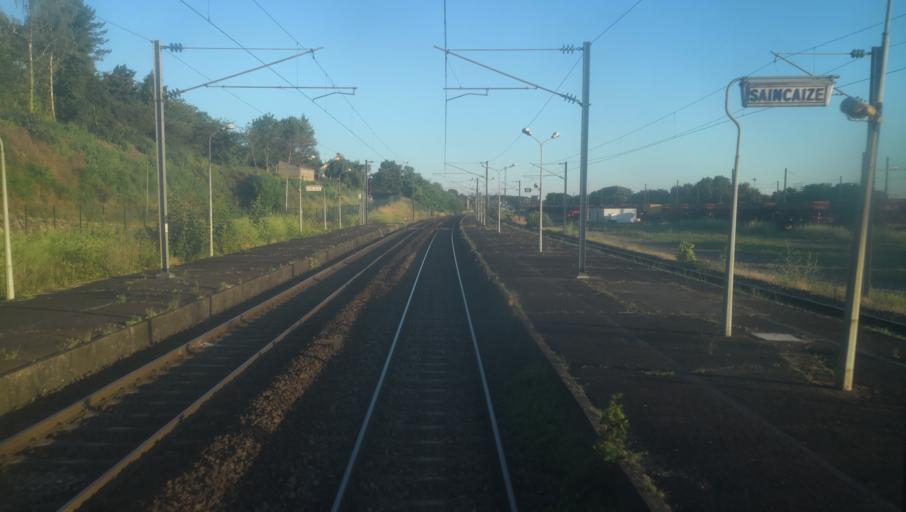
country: FR
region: Centre
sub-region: Departement du Cher
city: Cuffy
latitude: 46.9300
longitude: 3.0718
